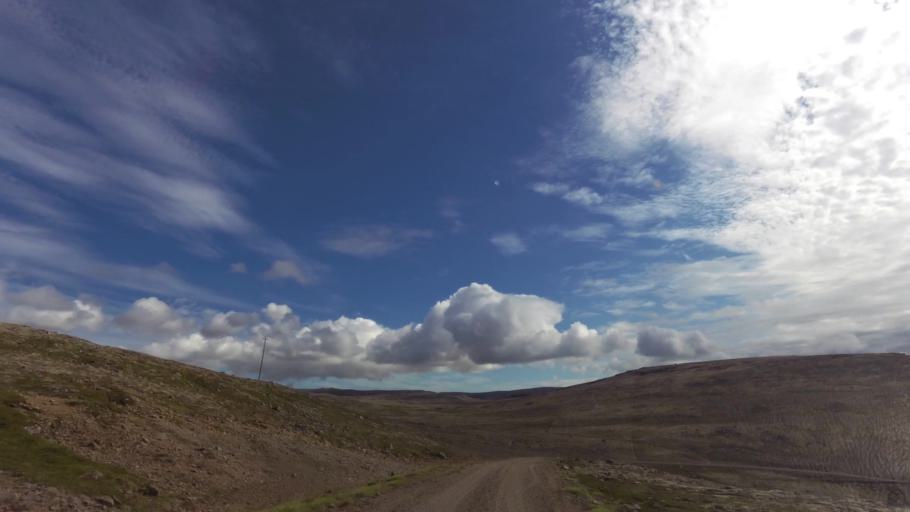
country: IS
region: West
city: Olafsvik
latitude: 65.6158
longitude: -24.3044
